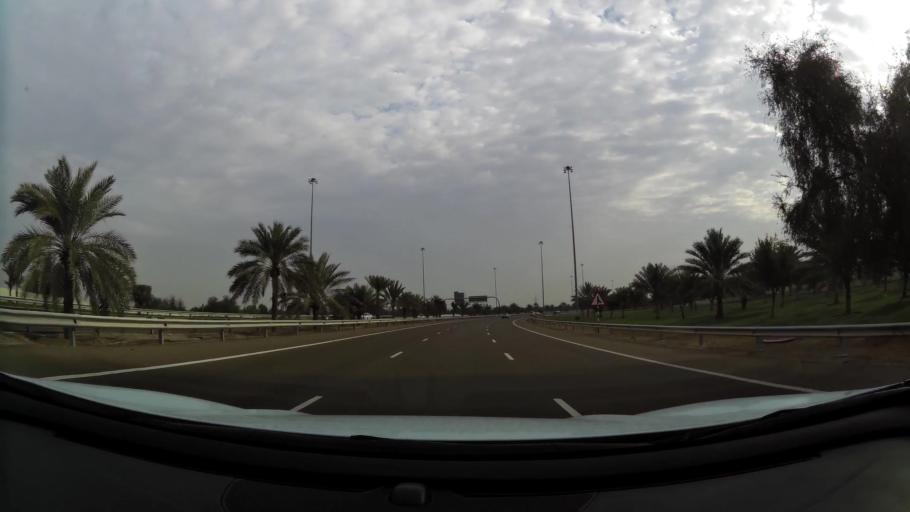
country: AE
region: Abu Dhabi
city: Al Ain
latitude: 24.1772
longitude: 55.1362
